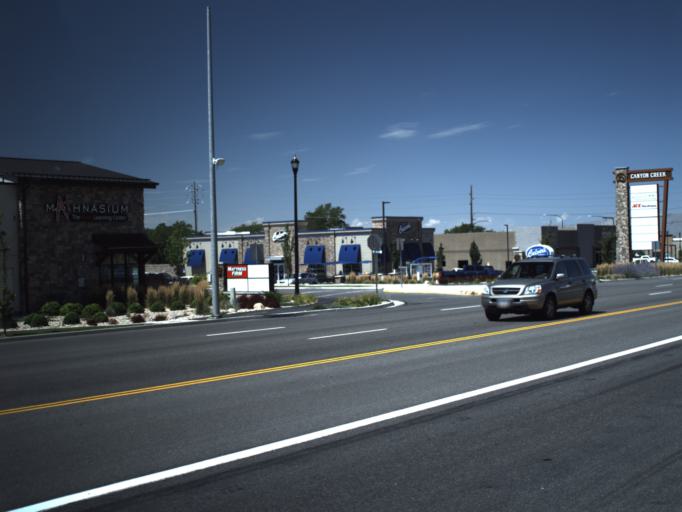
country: US
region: Utah
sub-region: Utah County
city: Spanish Fork
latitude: 40.1219
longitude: -111.6418
